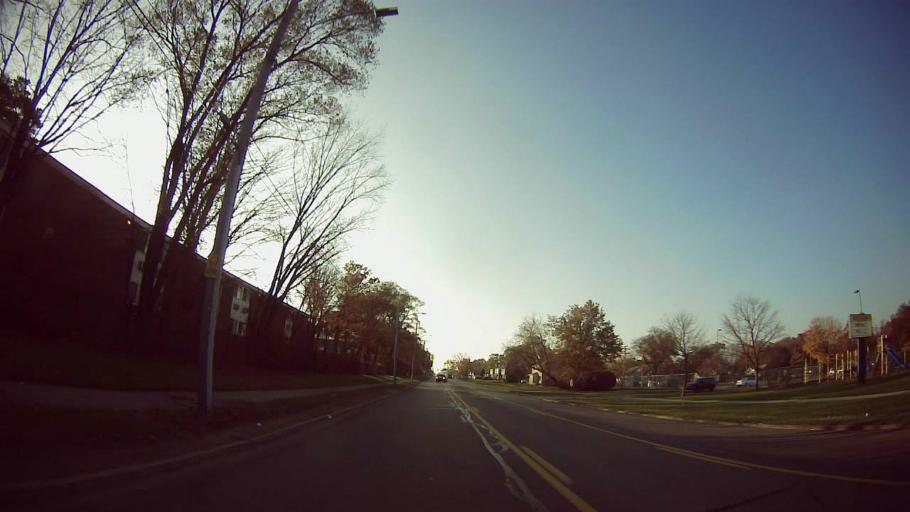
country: US
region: Michigan
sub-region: Oakland County
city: Oak Park
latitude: 42.4377
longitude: -83.1611
